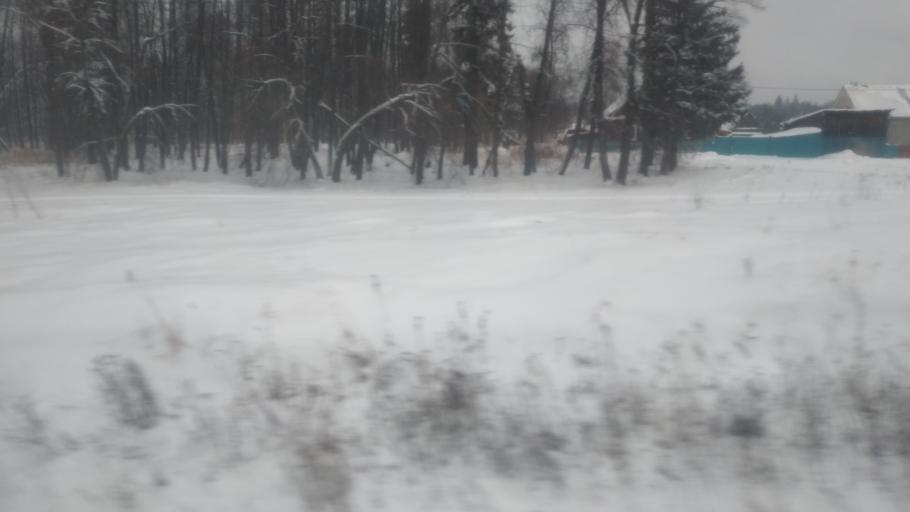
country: RU
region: Udmurtiya
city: Kama
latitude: 56.3214
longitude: 54.0945
